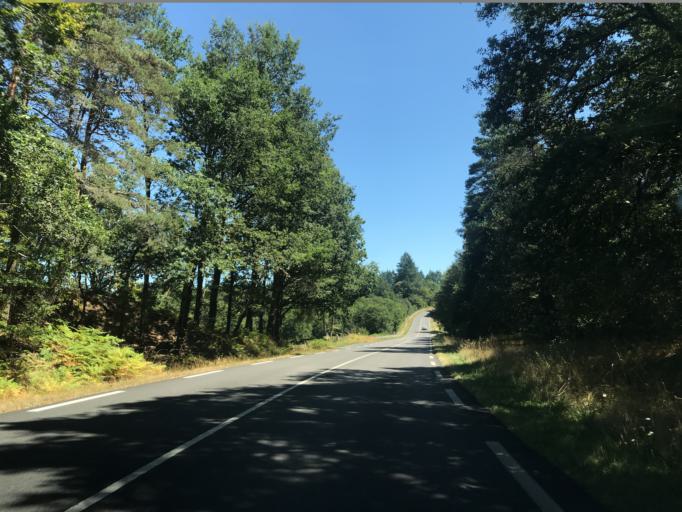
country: FR
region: Limousin
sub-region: Departement de la Correze
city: Correze
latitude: 45.3450
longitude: 1.9393
